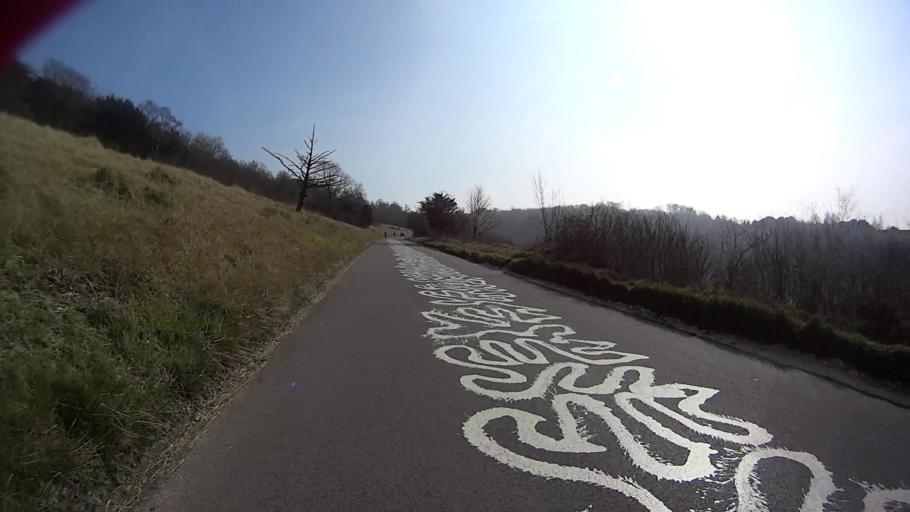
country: GB
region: England
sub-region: Surrey
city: Mickleham
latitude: 51.2552
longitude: -0.3136
